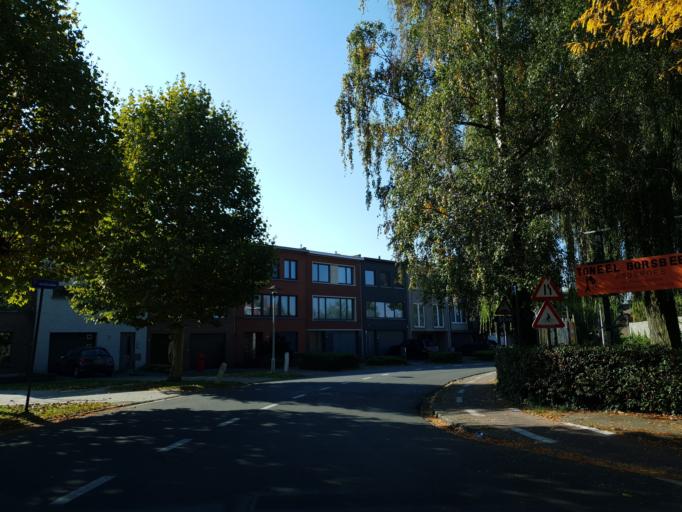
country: BE
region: Flanders
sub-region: Provincie Antwerpen
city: Borsbeek
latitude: 51.2005
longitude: 4.4822
